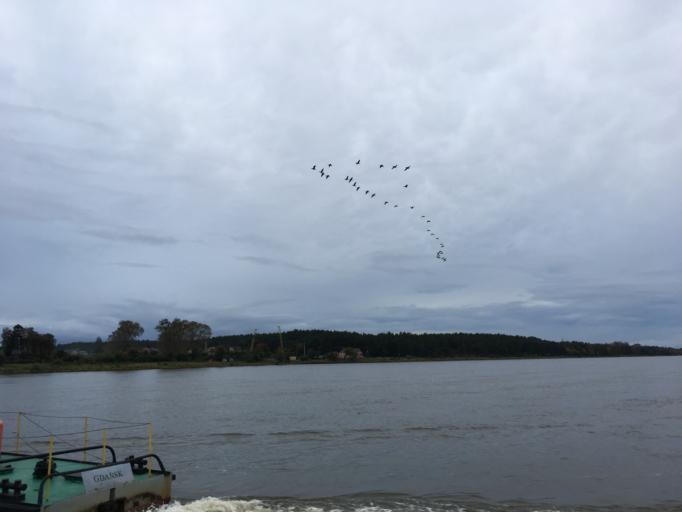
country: PL
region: Pomeranian Voivodeship
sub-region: Powiat nowodworski
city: Ostaszewo
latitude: 54.3331
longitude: 18.9408
